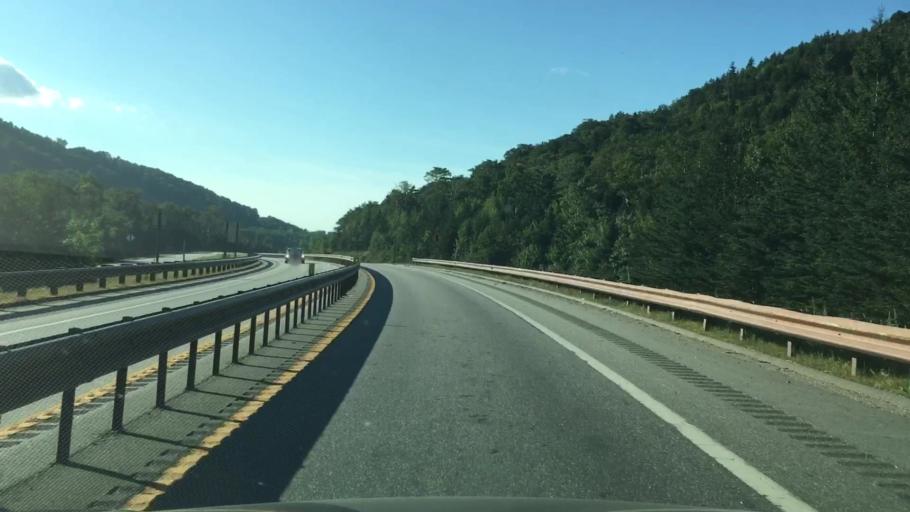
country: US
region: New Hampshire
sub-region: Grafton County
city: Deerfield
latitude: 44.1703
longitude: -71.6841
